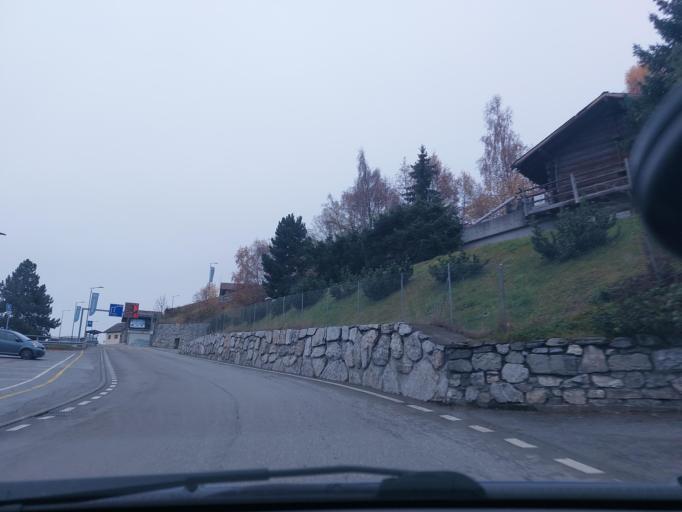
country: CH
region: Valais
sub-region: Conthey District
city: Basse-Nendaz
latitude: 46.1847
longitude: 7.2982
